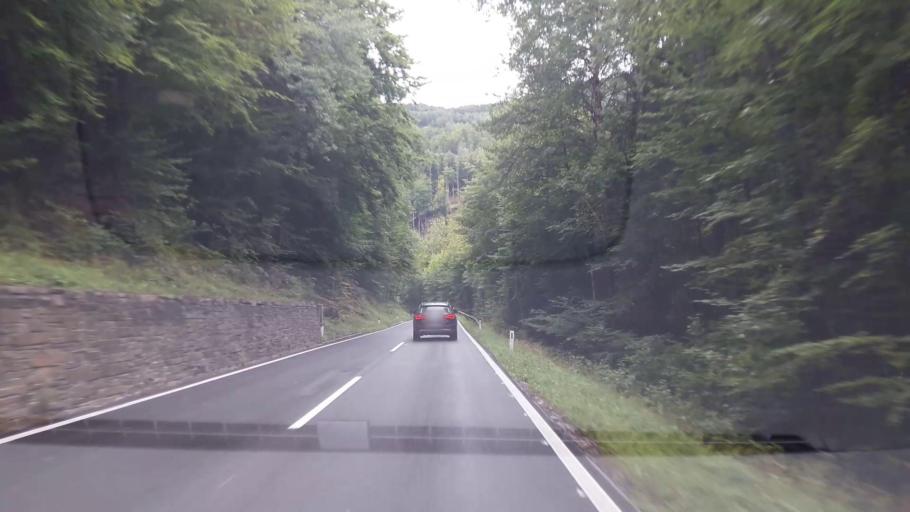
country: AT
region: Styria
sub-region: Politischer Bezirk Weiz
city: Floing
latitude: 47.2419
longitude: 15.7565
